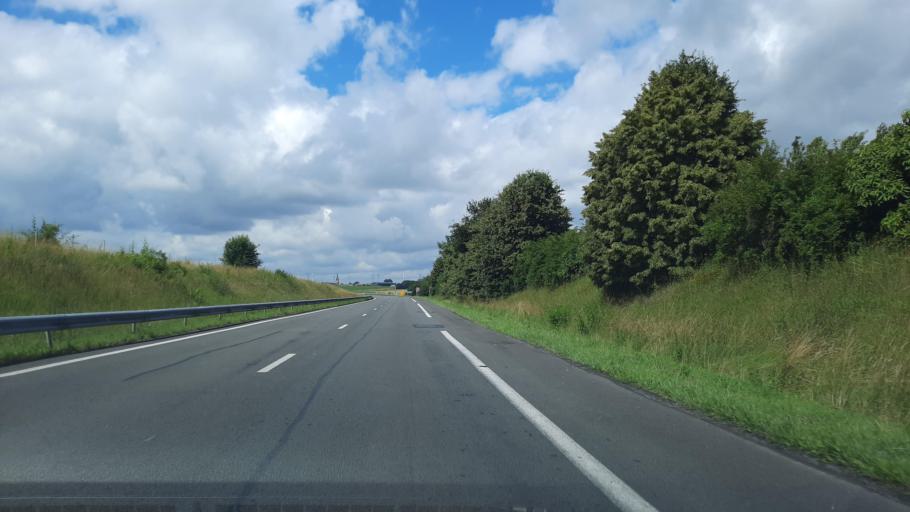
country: FR
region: Nord-Pas-de-Calais
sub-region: Departement du Nord
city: Fontaine-Notre-Dame
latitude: 50.1498
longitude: 3.1364
